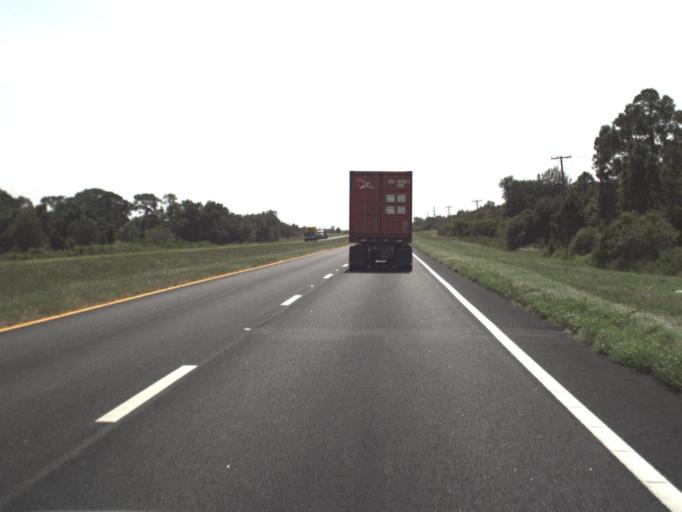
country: US
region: Florida
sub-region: Highlands County
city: Avon Park
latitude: 27.6648
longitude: -81.5443
